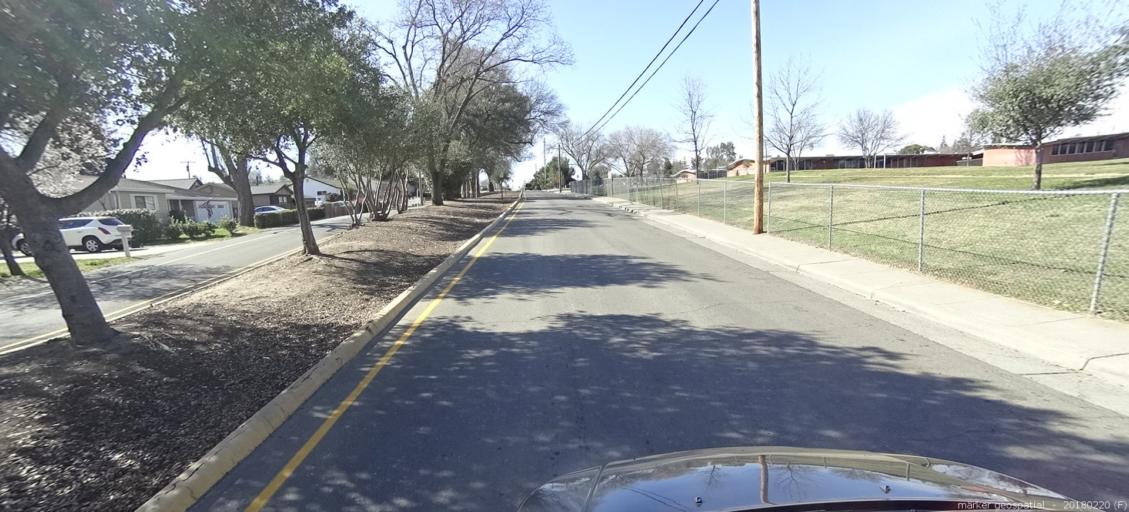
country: US
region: California
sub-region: Sacramento County
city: Orangevale
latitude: 38.6930
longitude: -121.2211
